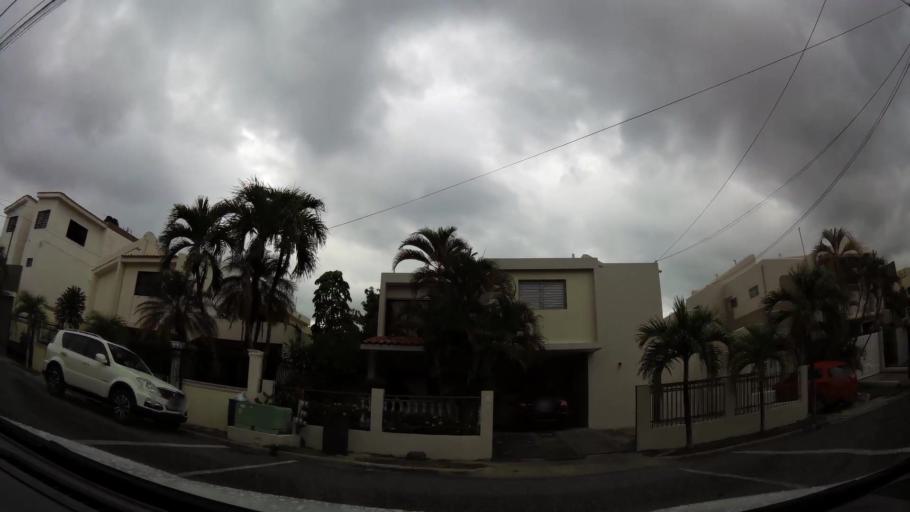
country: DO
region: Nacional
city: La Agustina
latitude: 18.4888
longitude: -69.9374
